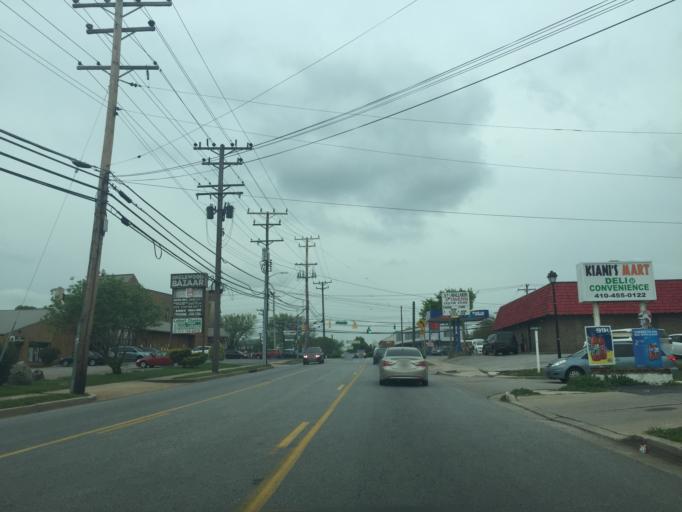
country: US
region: Maryland
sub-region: Baltimore County
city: Catonsville
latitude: 39.2935
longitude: -76.7304
